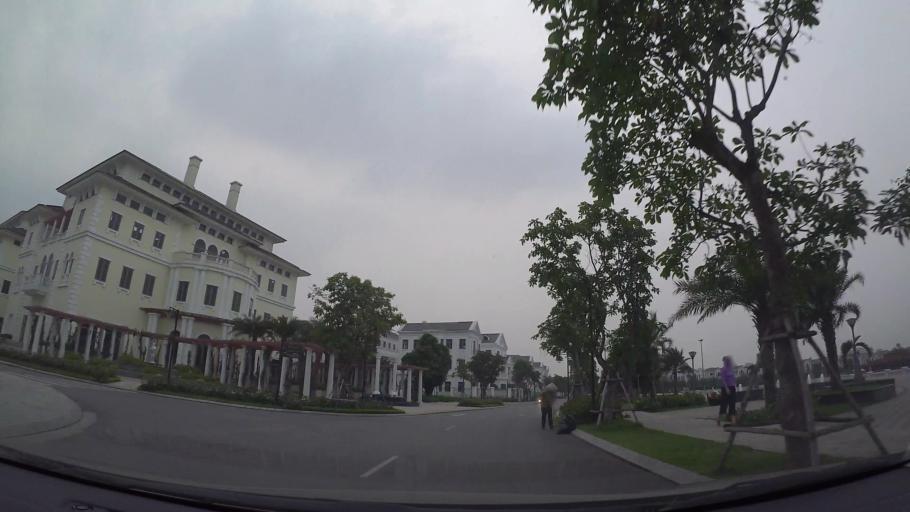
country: VN
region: Ha Noi
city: Trau Quy
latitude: 21.0468
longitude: 105.9055
